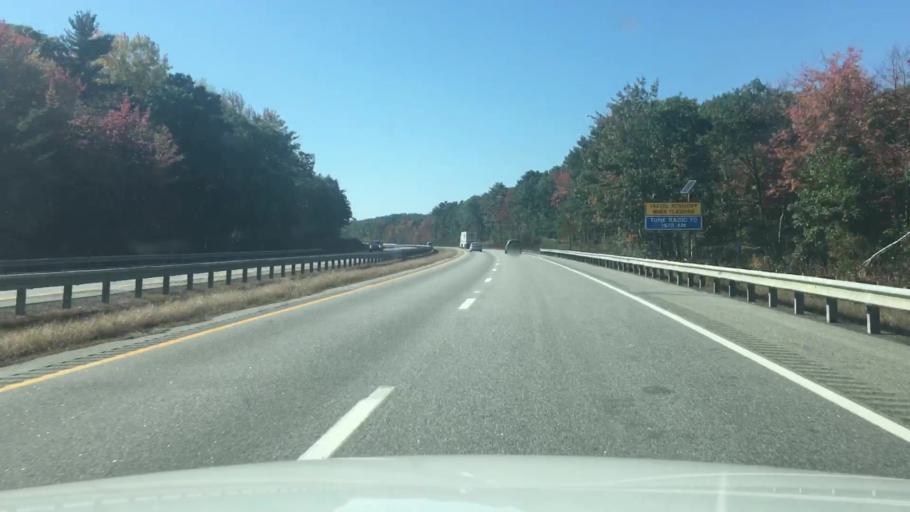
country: US
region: Maine
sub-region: Cumberland County
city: Falmouth
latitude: 43.7344
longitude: -70.2418
